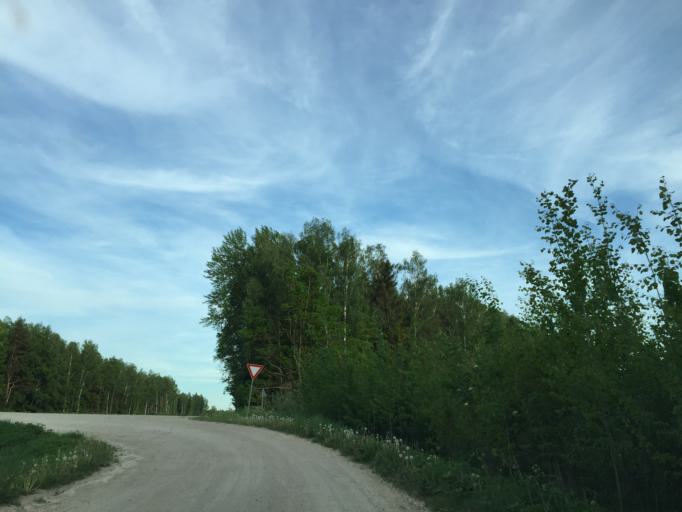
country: LV
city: Tireli
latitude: 56.6783
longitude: 23.5034
